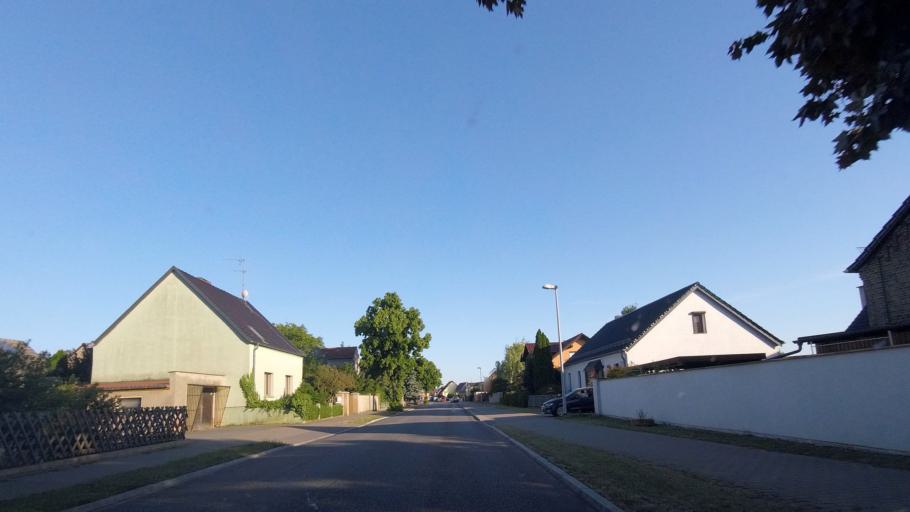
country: DE
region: Brandenburg
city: Golzow
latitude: 52.2819
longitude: 12.6038
